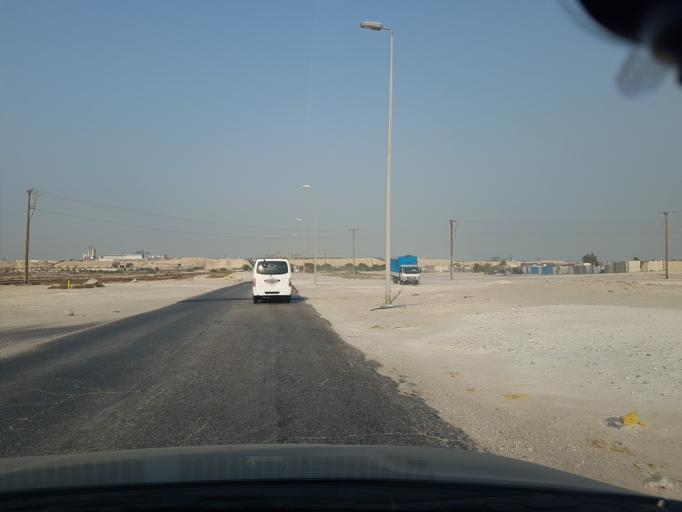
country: BH
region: Northern
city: Ar Rifa'
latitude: 26.0892
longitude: 50.5761
